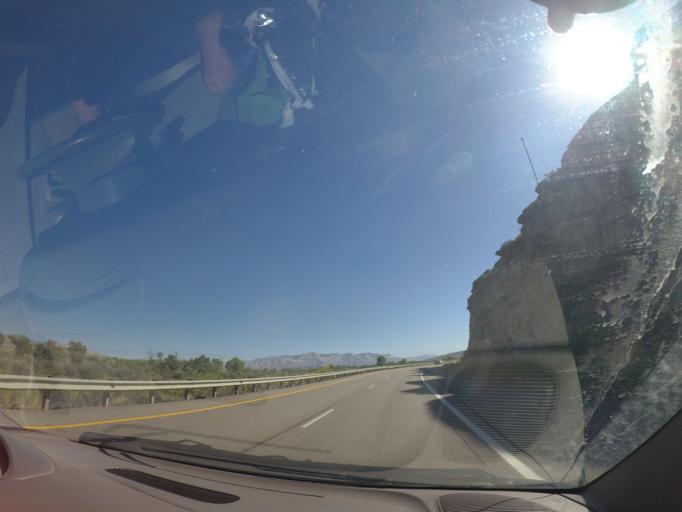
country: US
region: Colorado
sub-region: Mesa County
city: Palisade
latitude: 39.2715
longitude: -108.2481
